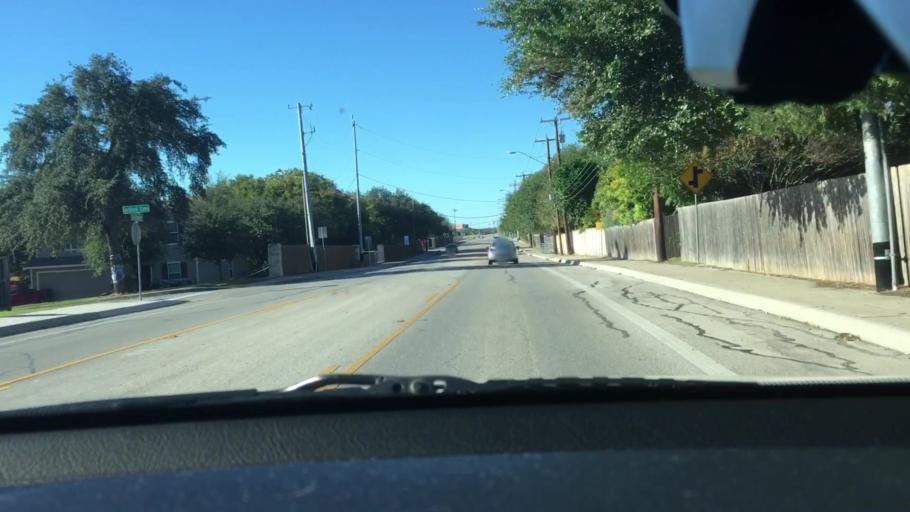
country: US
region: Texas
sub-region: Bexar County
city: Converse
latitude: 29.5366
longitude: -98.3152
